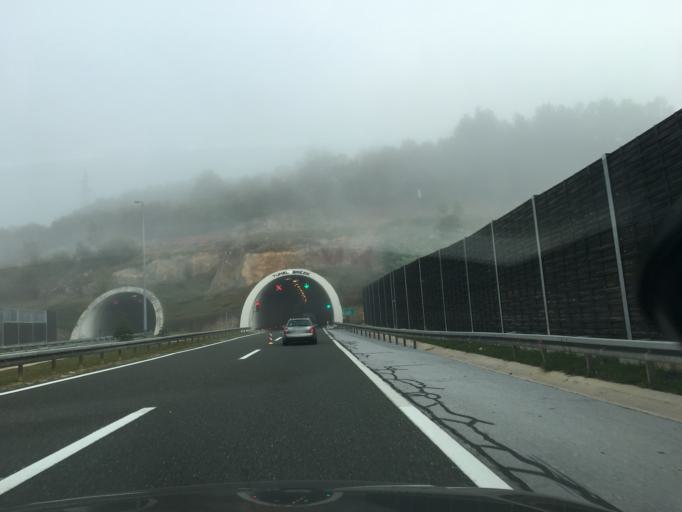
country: HR
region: Licko-Senjska
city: Otocac
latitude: 44.8695
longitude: 15.2076
